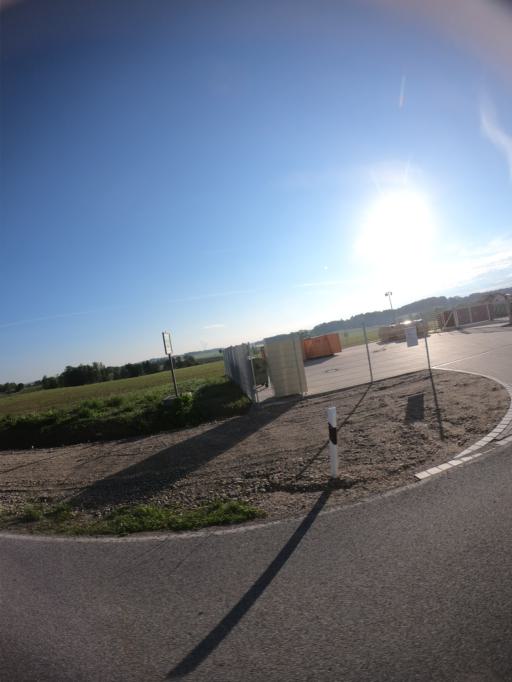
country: DE
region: Bavaria
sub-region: Upper Bavaria
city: Bockhorn
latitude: 48.3176
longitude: 11.9831
